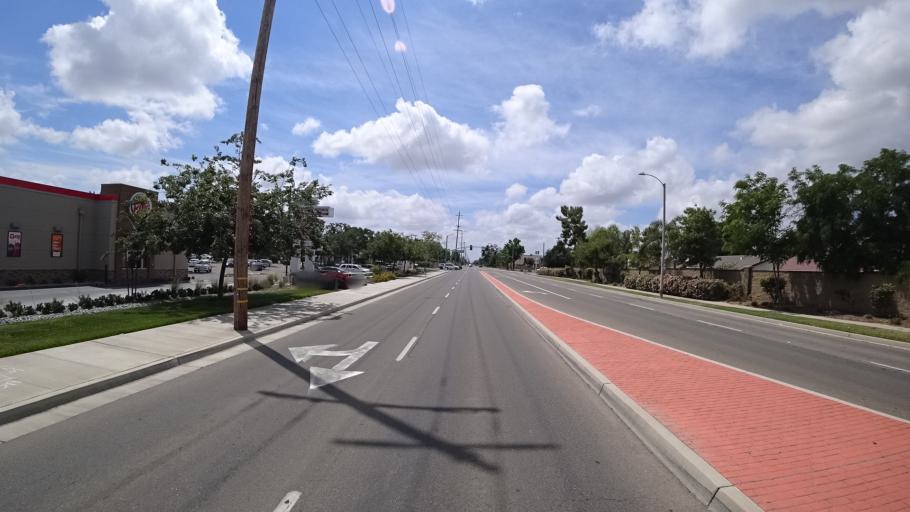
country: US
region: California
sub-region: Kings County
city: Lucerne
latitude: 36.3582
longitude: -119.6551
